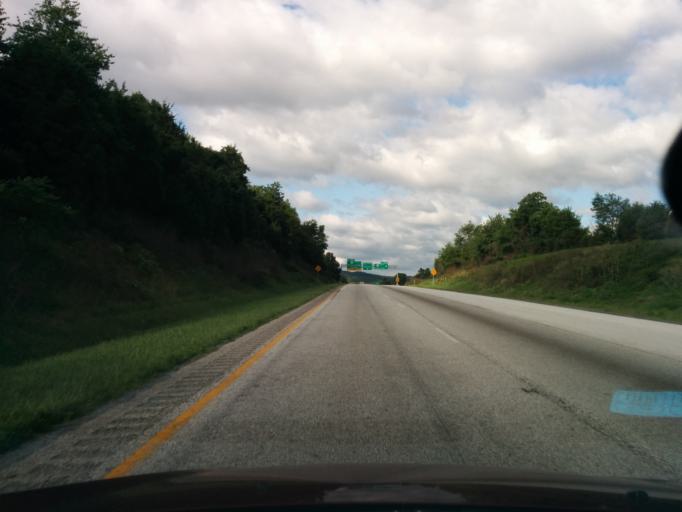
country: US
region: Virginia
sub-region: Rockbridge County
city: Glasgow
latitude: 37.6761
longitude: -79.4998
